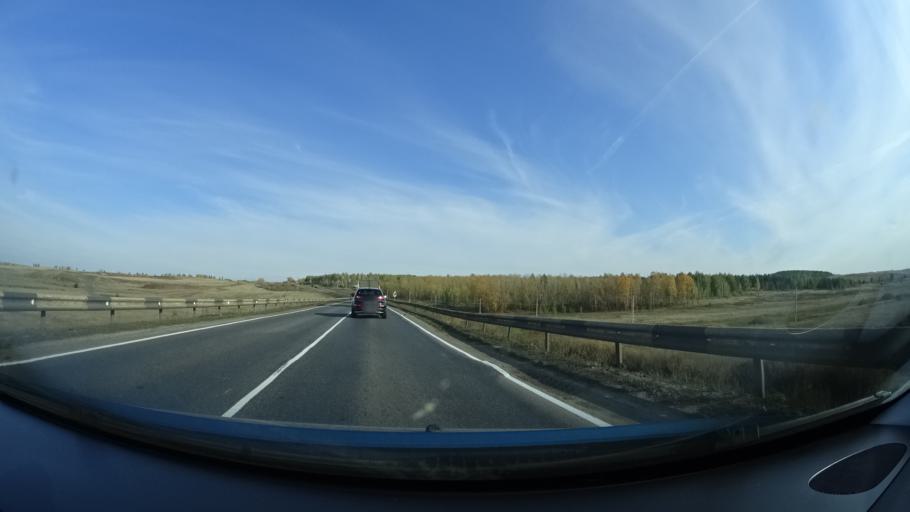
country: RU
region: Bashkortostan
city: Buzdyak
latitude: 54.6600
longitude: 54.6747
